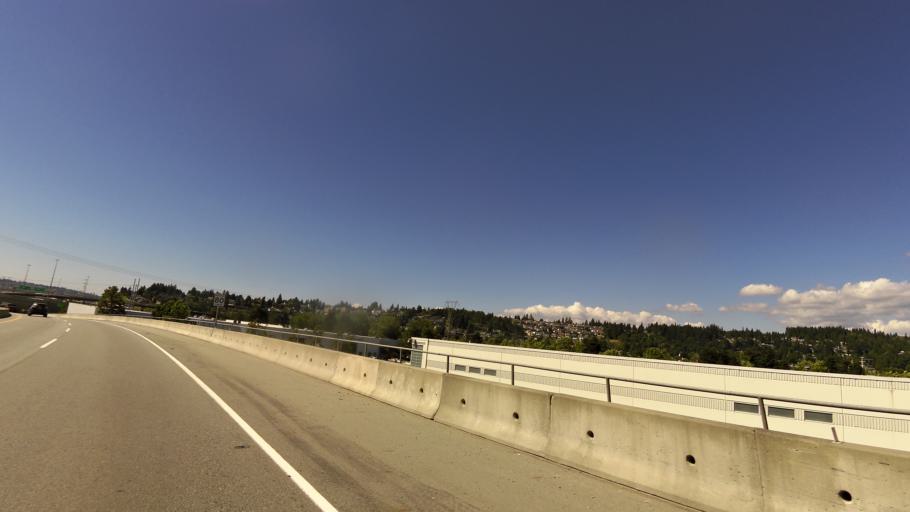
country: CA
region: British Columbia
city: Port Moody
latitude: 49.2283
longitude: -122.8202
